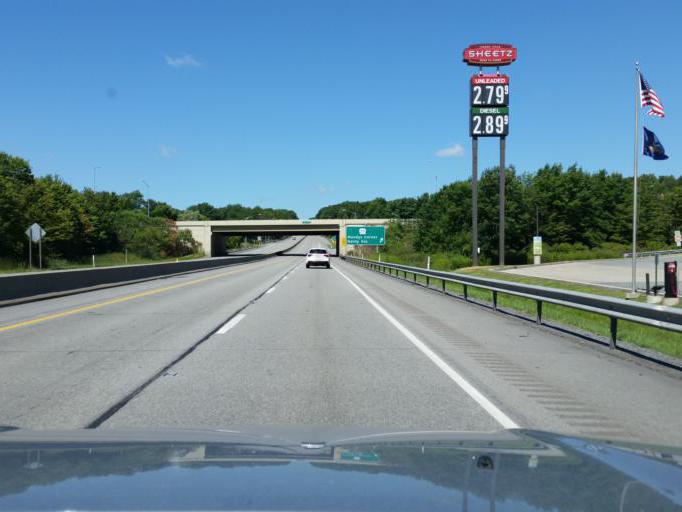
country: US
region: Pennsylvania
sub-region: Cambria County
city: Mundys Corner
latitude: 40.4499
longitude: -78.8375
